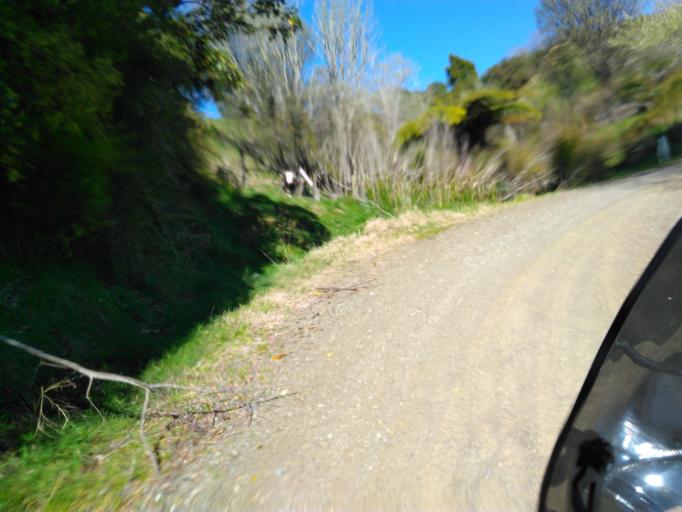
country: NZ
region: Bay of Plenty
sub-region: Opotiki District
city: Opotiki
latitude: -38.3735
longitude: 177.6070
